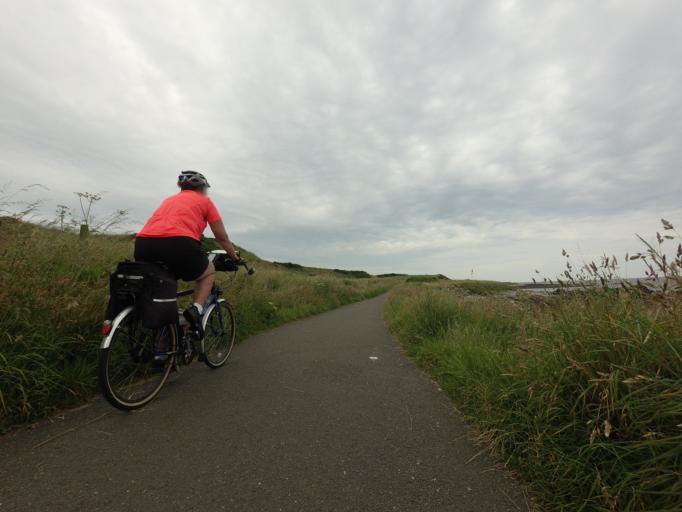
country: GB
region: Scotland
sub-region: Aberdeenshire
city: Whitehills
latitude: 57.6749
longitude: -2.5672
